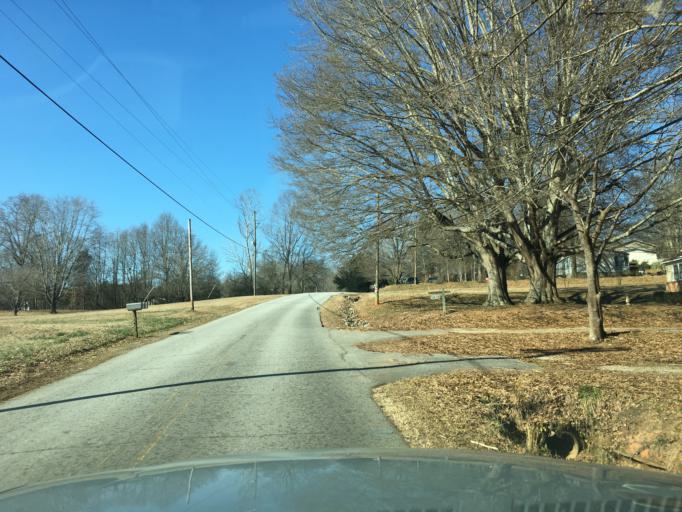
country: US
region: South Carolina
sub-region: Pickens County
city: Arial
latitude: 34.8727
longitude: -82.6454
